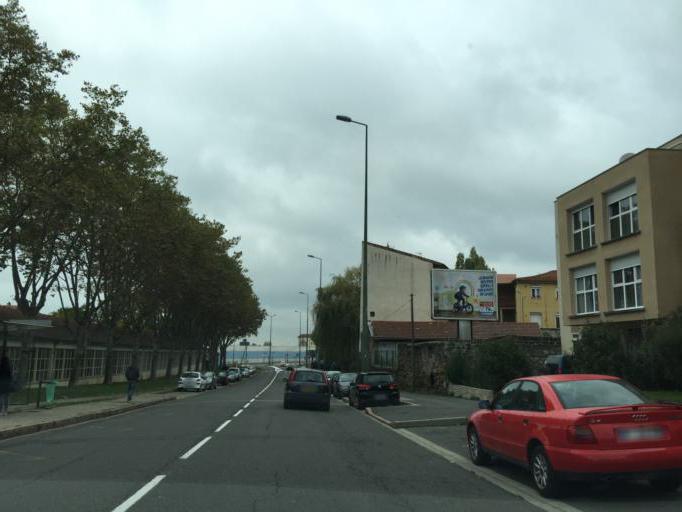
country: FR
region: Rhone-Alpes
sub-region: Departement de la Loire
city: Saint-Etienne
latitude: 45.4514
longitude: 4.4008
